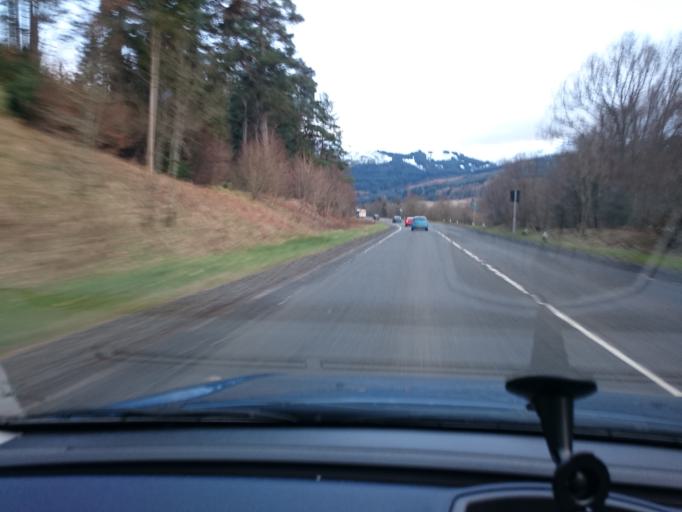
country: GB
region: Scotland
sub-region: Stirling
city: Callander
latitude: 56.3172
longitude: -4.3294
